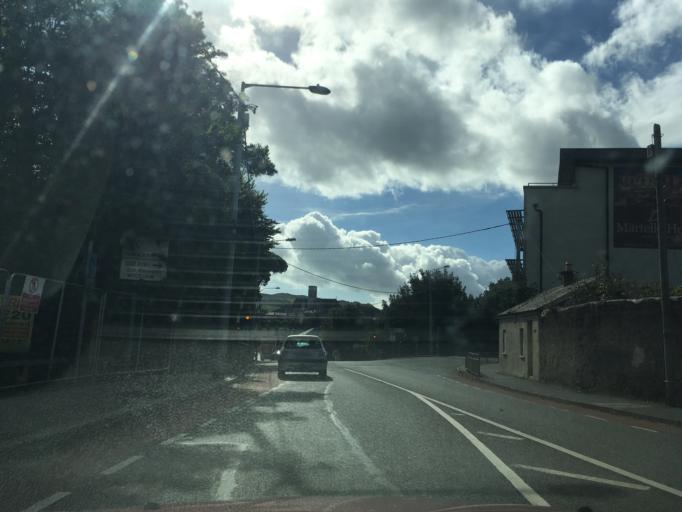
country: IE
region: Leinster
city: Little Bray
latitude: 53.2081
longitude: -6.1144
